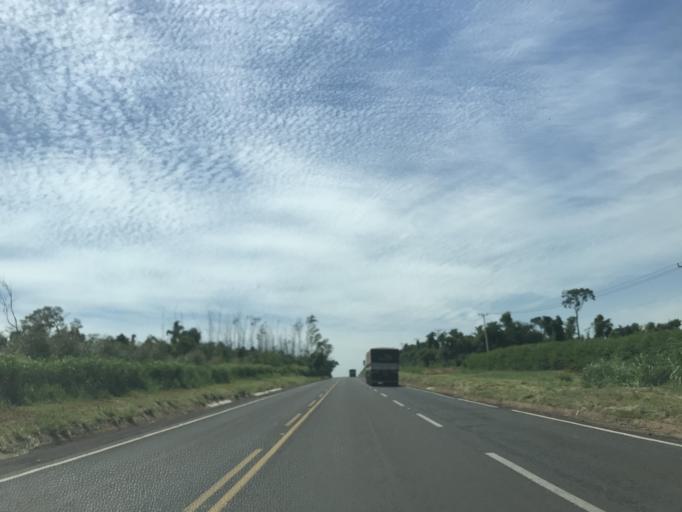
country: BR
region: Parana
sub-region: Paranavai
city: Nova Aurora
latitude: -22.9618
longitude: -52.6460
